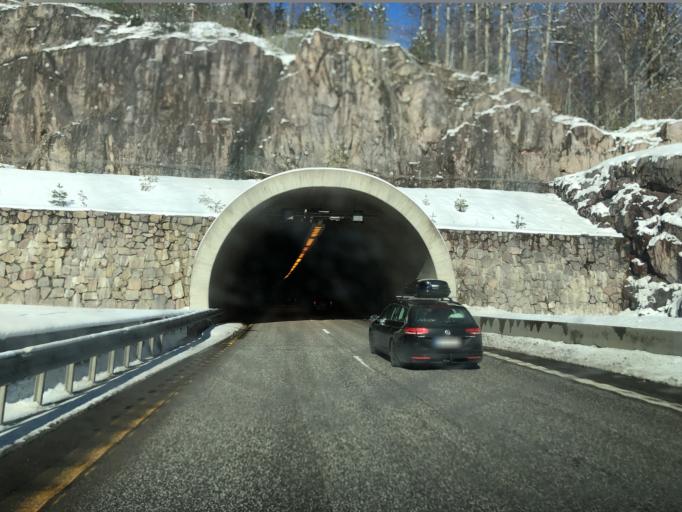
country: NO
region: Vestfold
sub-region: Horten
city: Skoppum
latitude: 59.3895
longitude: 10.3740
